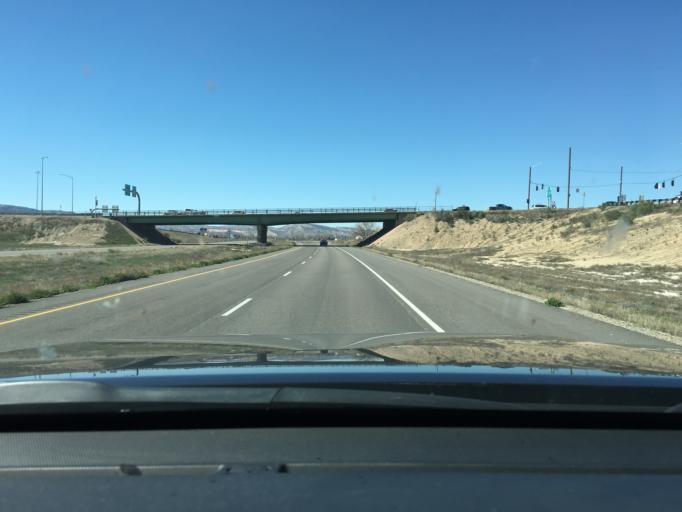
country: US
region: Colorado
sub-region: Mesa County
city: Fruita
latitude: 39.1551
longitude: -108.7356
